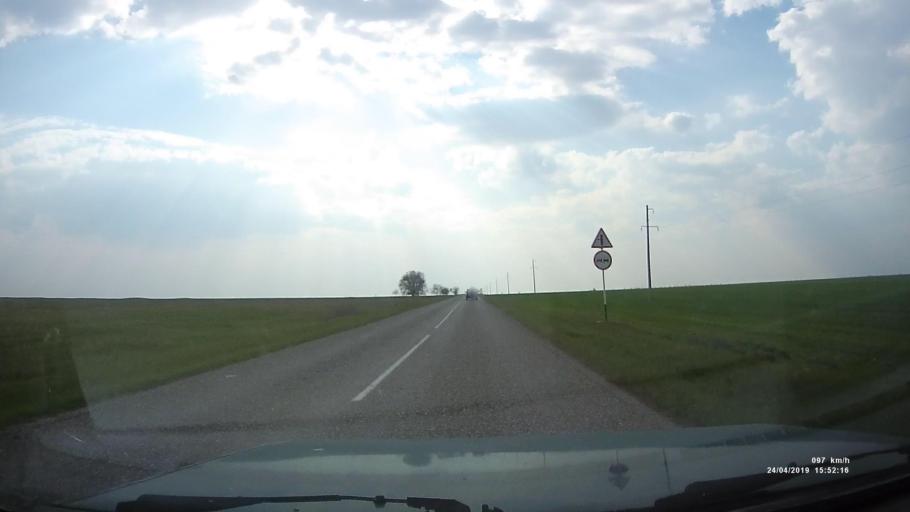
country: RU
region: Kalmykiya
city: Yashalta
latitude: 46.6043
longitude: 42.5915
